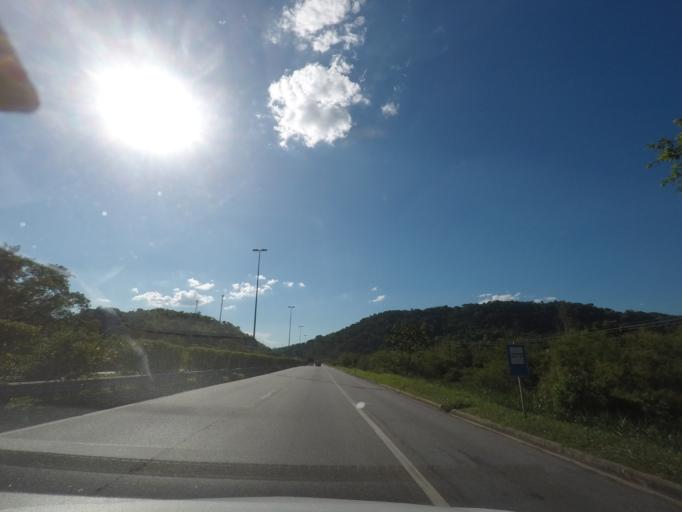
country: BR
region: Rio de Janeiro
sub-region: Petropolis
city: Petropolis
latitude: -22.6556
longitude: -43.1390
